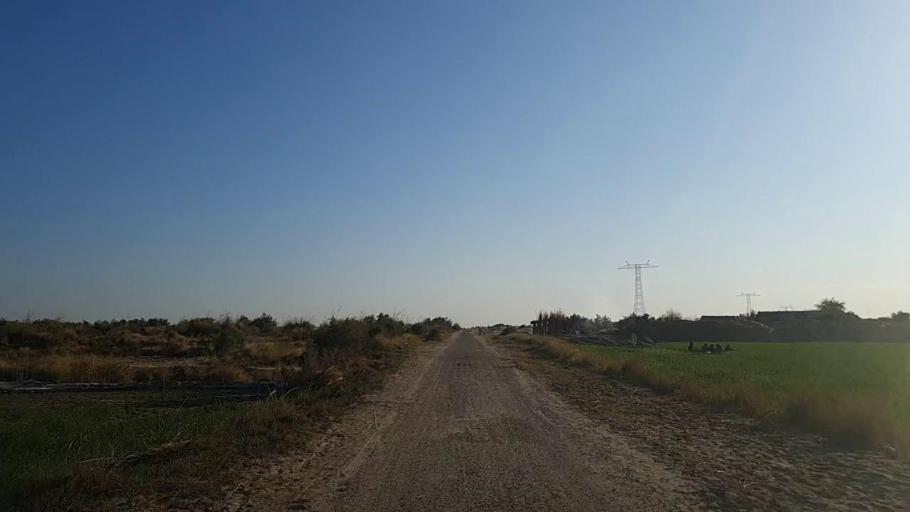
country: PK
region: Sindh
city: Khadro
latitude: 26.2669
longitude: 68.8602
